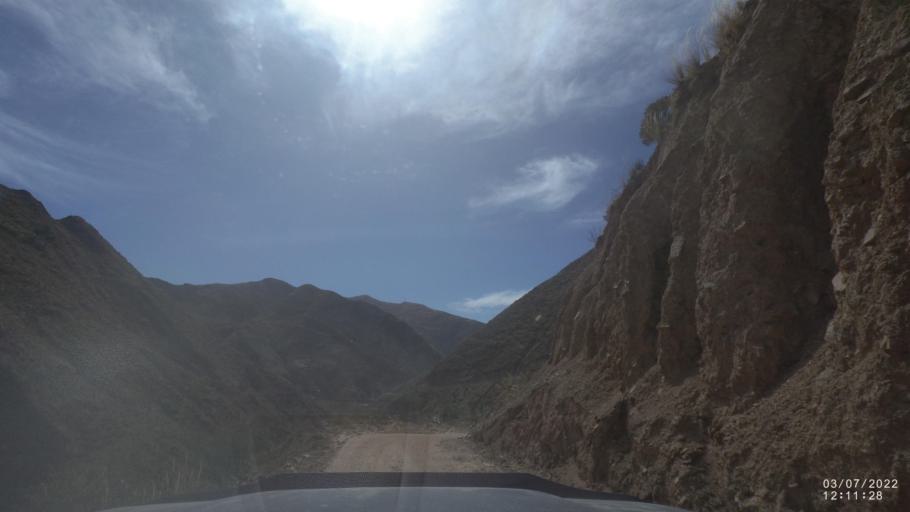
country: BO
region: Cochabamba
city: Irpa Irpa
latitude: -17.8405
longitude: -66.6142
